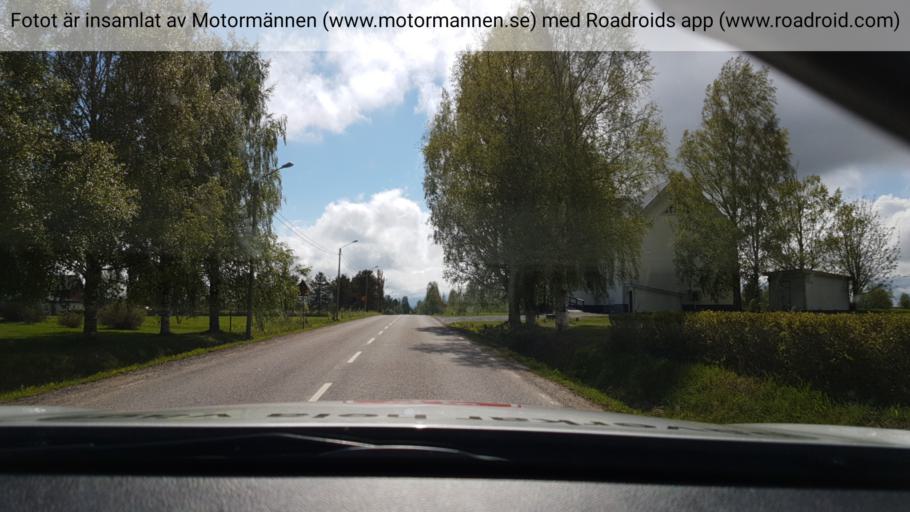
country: SE
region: Vaesterbotten
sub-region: Vannas Kommun
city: Vannasby
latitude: 63.9793
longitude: 19.8905
